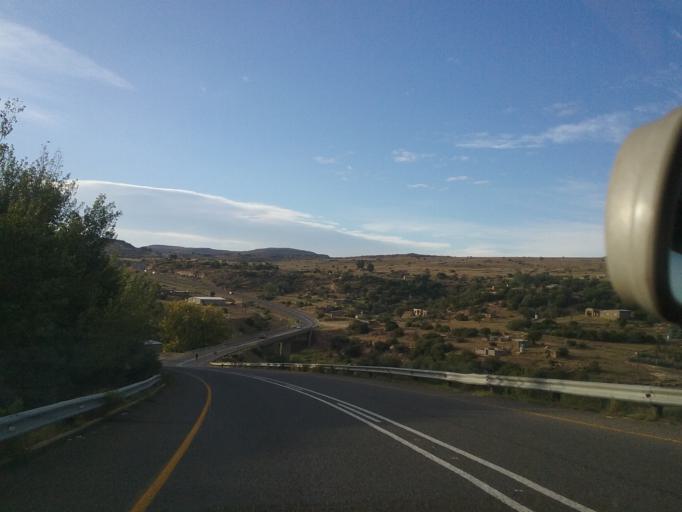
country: LS
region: Mohale's Hoek District
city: Mohale's Hoek
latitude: -30.2796
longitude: 27.4552
